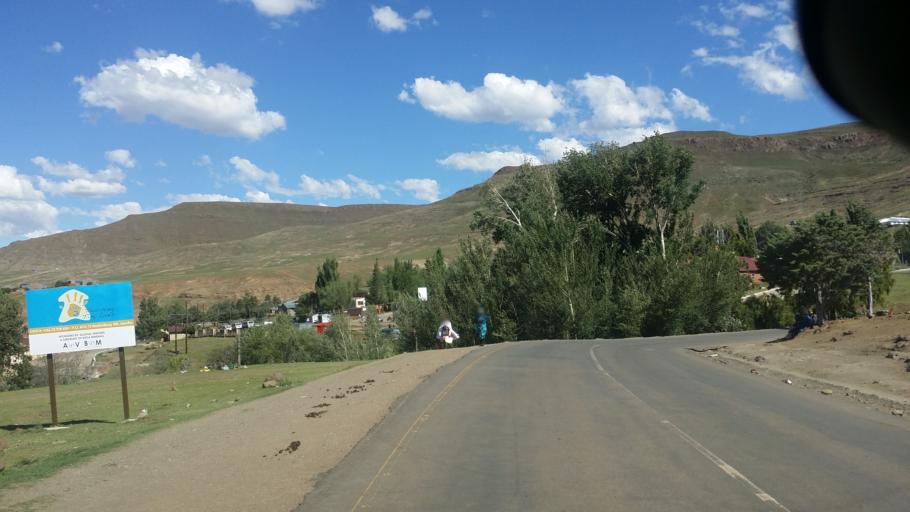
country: LS
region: Mokhotlong
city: Mokhotlong
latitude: -29.2894
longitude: 29.0721
